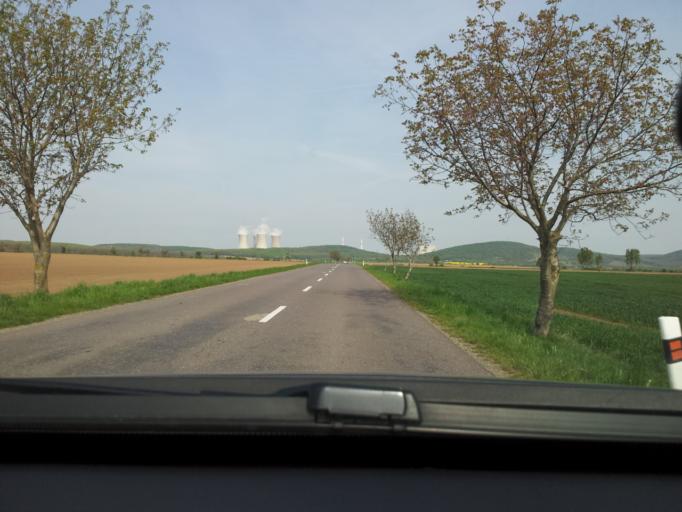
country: SK
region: Nitriansky
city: Tlmace
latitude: 48.2263
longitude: 18.4940
